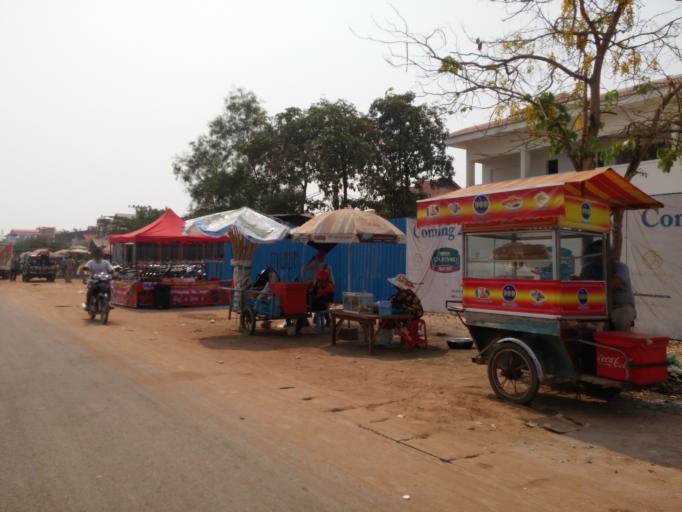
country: KH
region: Siem Reap
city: Siem Reap
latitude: 13.3593
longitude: 103.8812
